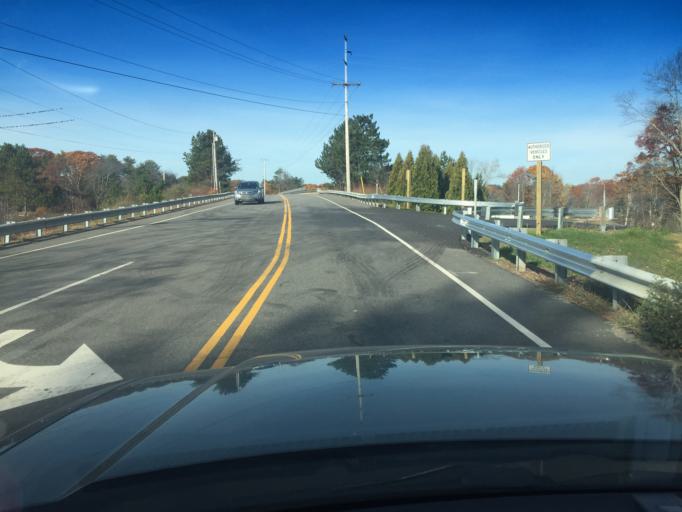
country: US
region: Maine
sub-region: York County
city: York Harbor
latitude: 43.1511
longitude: -70.6746
